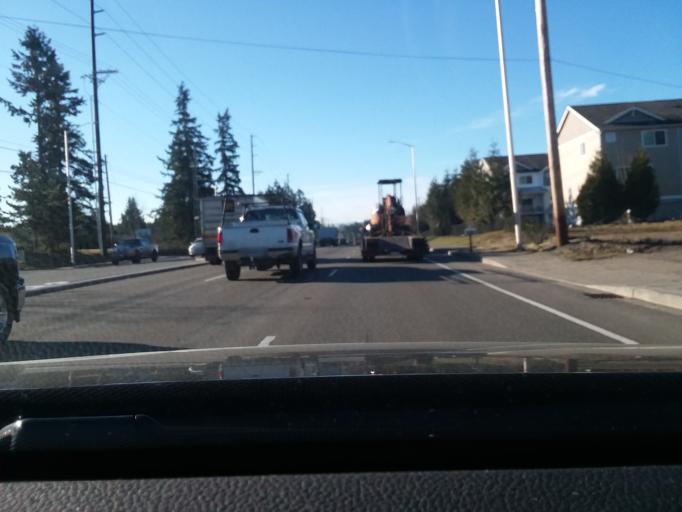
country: US
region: Washington
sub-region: Pierce County
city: Frederickson
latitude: 47.1081
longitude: -122.3578
